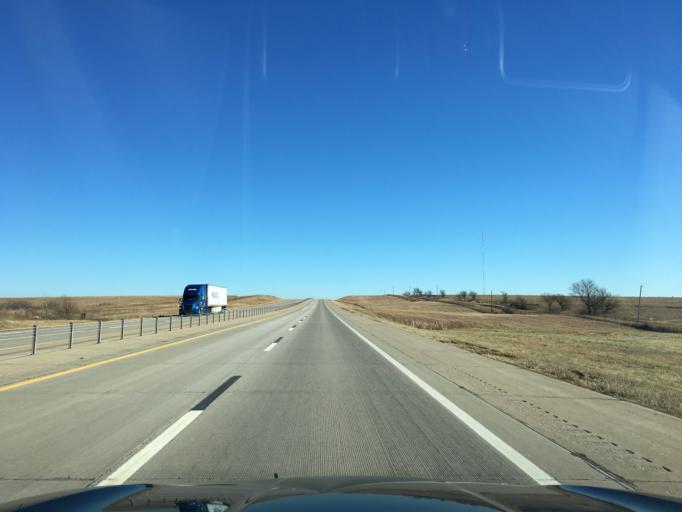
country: US
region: Oklahoma
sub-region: Noble County
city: Perry
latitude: 36.3920
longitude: -97.1576
